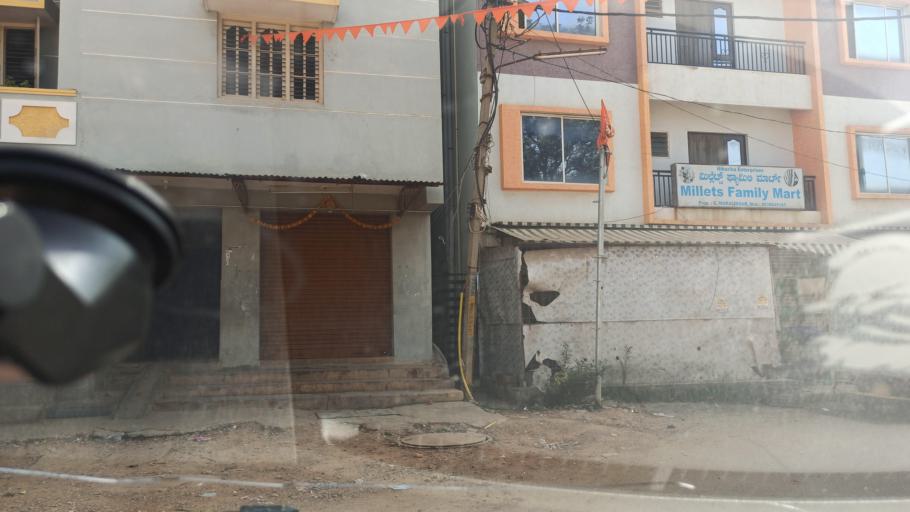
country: IN
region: Karnataka
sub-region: Bangalore Urban
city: Yelahanka
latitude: 13.0664
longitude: 77.5917
